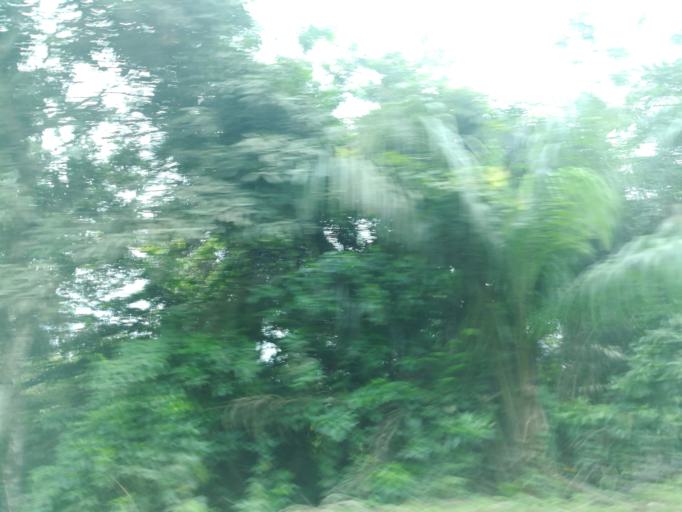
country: NG
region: Lagos
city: Ejirin
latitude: 6.6457
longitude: 3.7750
